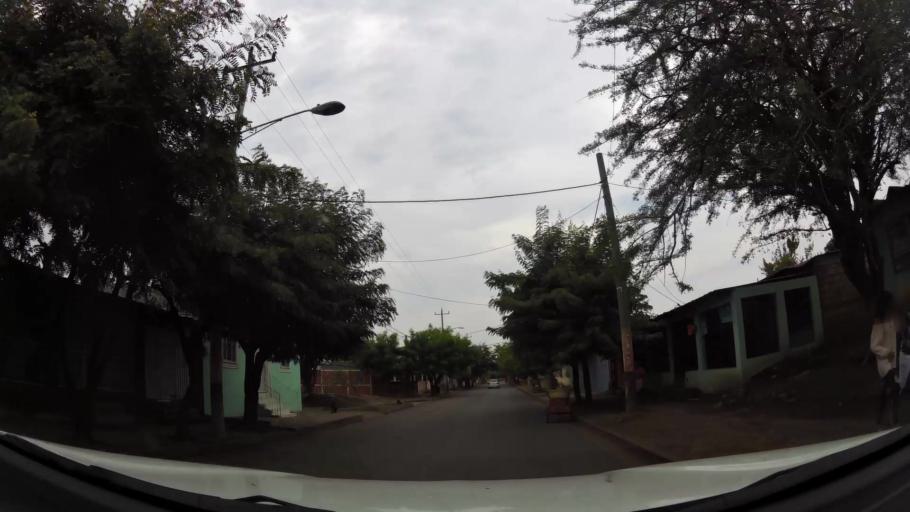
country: NI
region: Granada
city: Granada
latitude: 11.9480
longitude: -85.9499
